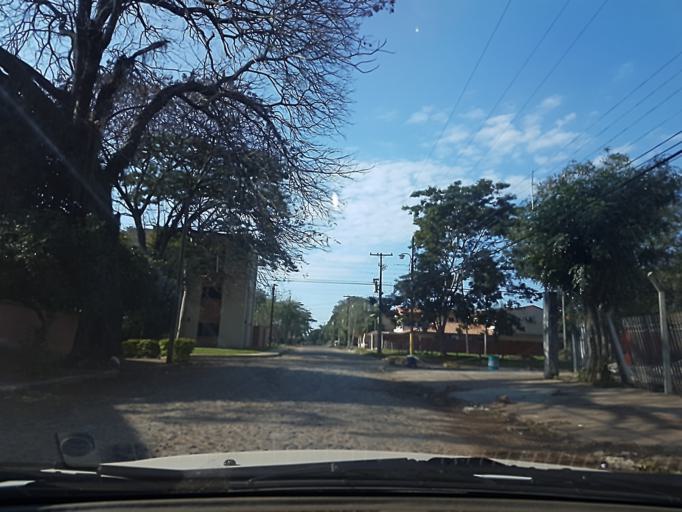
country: PY
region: Central
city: Colonia Mariano Roque Alonso
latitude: -25.2403
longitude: -57.5399
